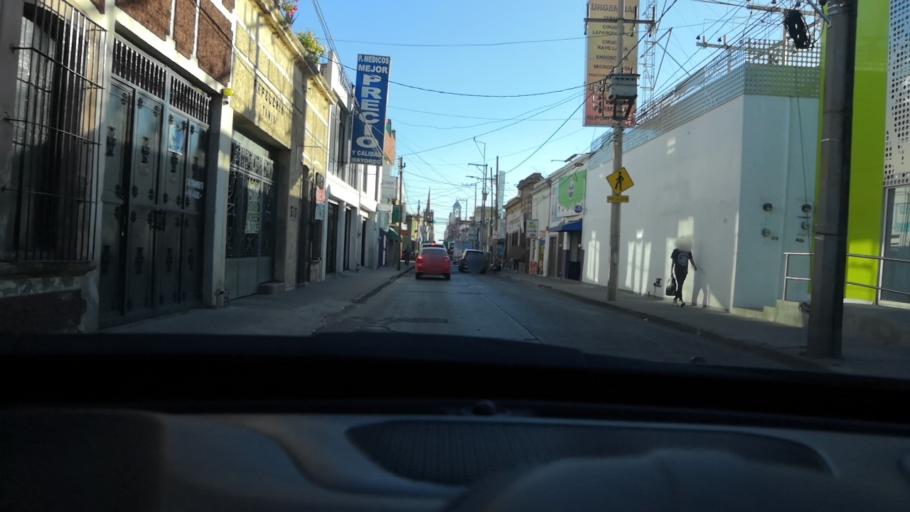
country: MX
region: Guanajuato
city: Leon
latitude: 21.1278
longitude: -101.6819
